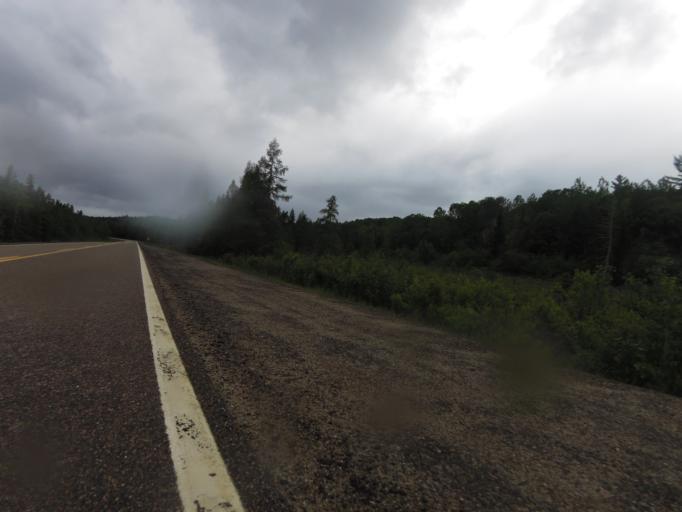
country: CA
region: Quebec
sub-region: Outaouais
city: Shawville
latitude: 45.9206
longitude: -76.2526
